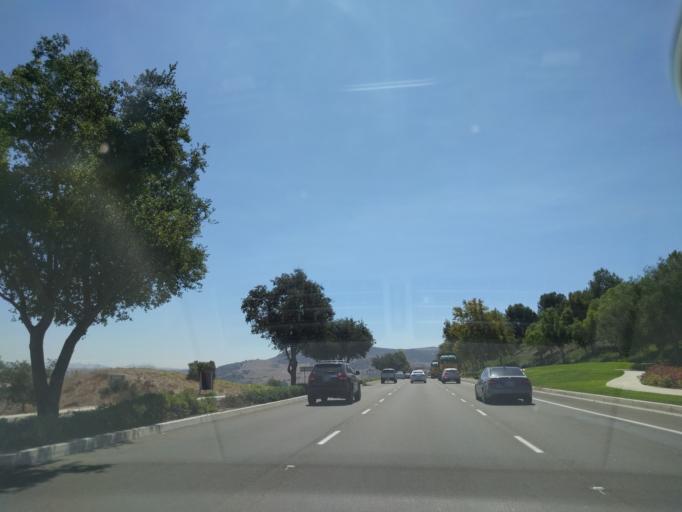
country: US
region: California
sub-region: Orange County
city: Ladera Ranch
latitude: 33.5396
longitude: -117.6265
